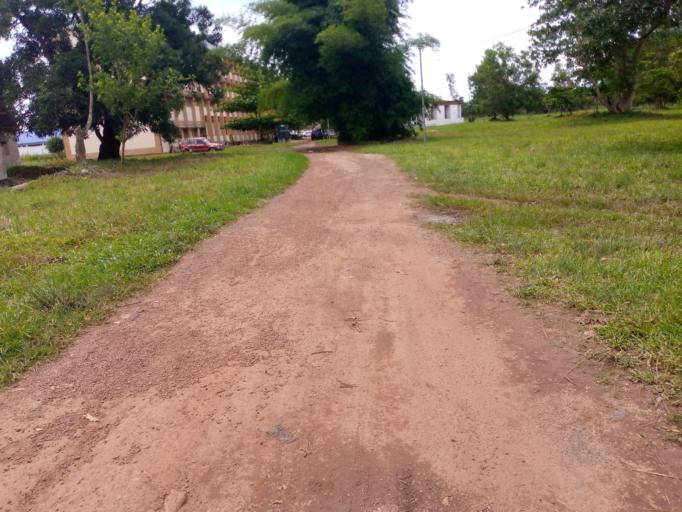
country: SL
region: Southern Province
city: Largo
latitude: 8.1162
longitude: -12.0686
